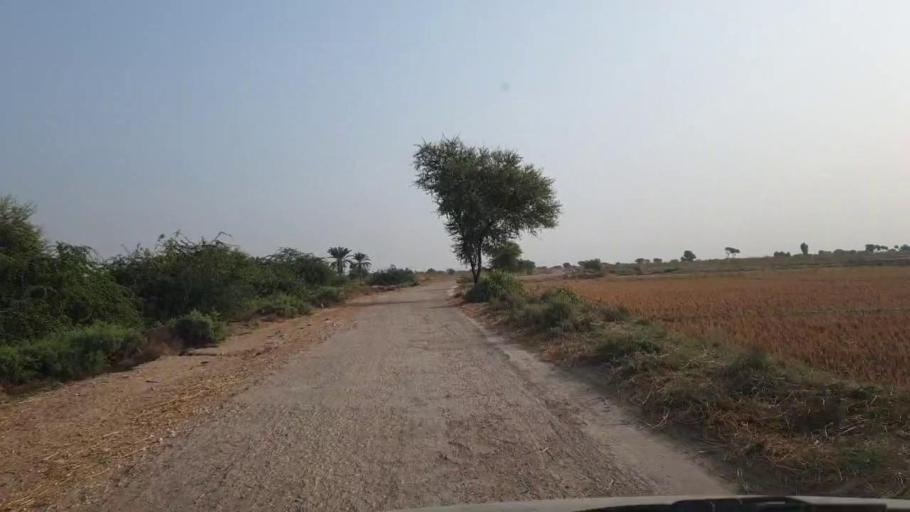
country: PK
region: Sindh
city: Matli
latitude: 25.0605
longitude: 68.7614
